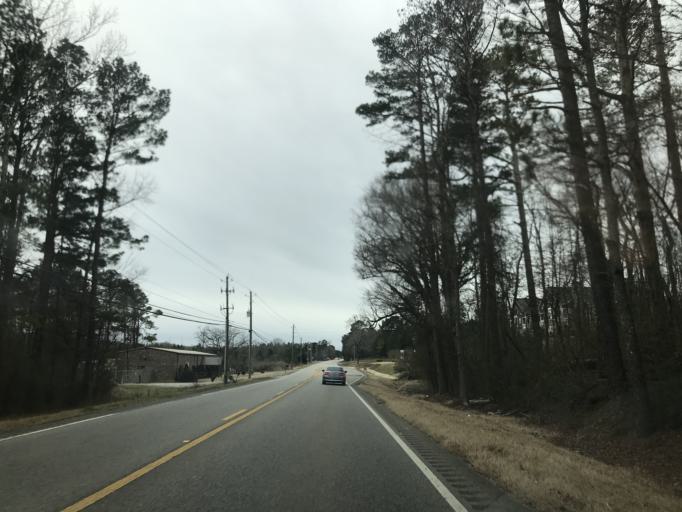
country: US
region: Alabama
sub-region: Shelby County
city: Brook Highland
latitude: 33.4413
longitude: -86.6594
